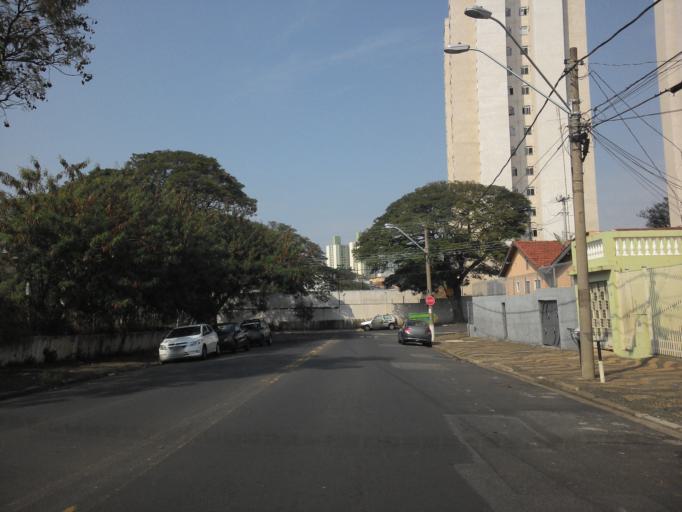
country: BR
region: Sao Paulo
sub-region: Campinas
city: Campinas
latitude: -22.9123
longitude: -47.0851
